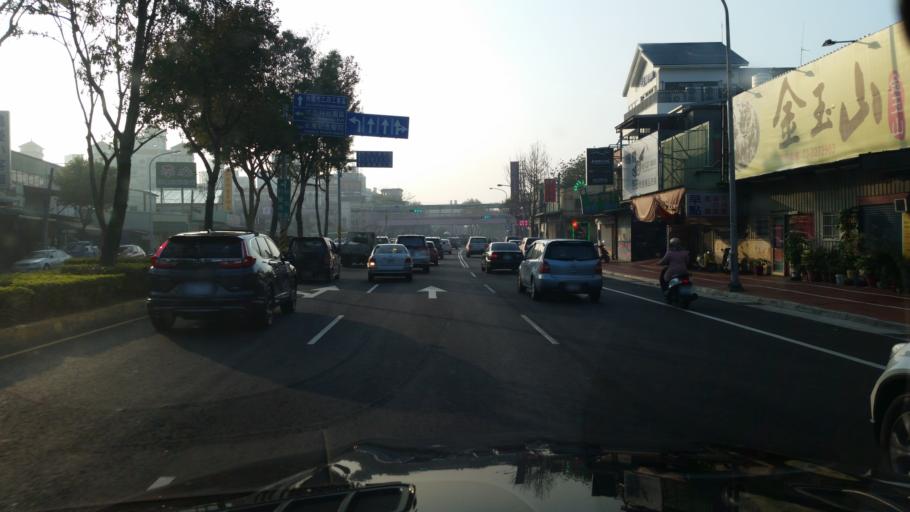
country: TW
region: Taiwan
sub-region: Taoyuan
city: Taoyuan
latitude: 25.0547
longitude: 121.3582
